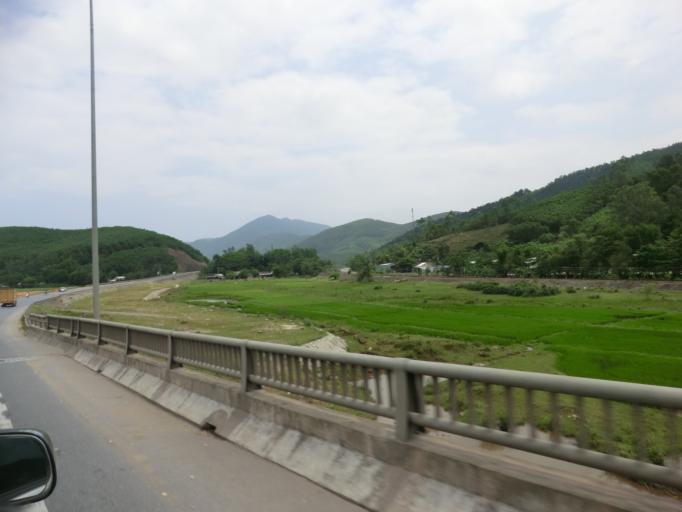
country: VN
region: Thua Thien-Hue
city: Phu Loc
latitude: 16.2763
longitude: 107.8987
